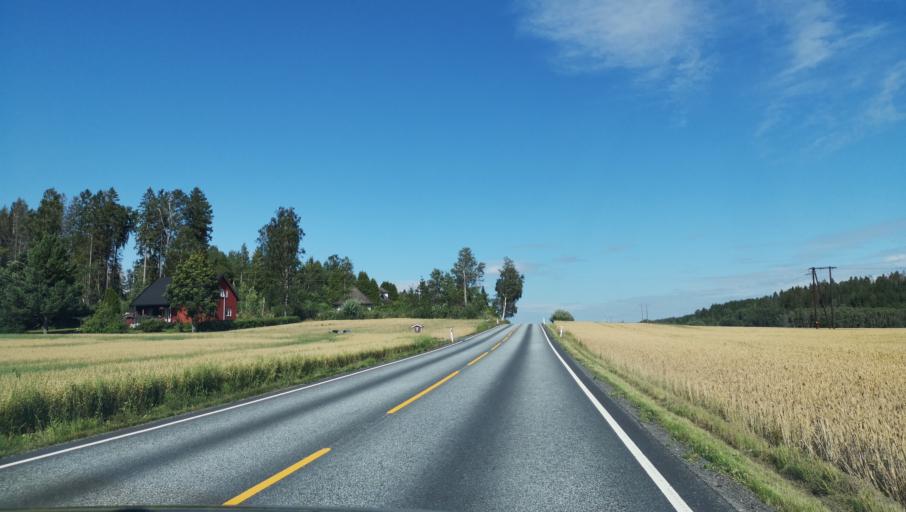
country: NO
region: Ostfold
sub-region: Hobol
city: Elvestad
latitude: 59.6005
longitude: 10.9058
